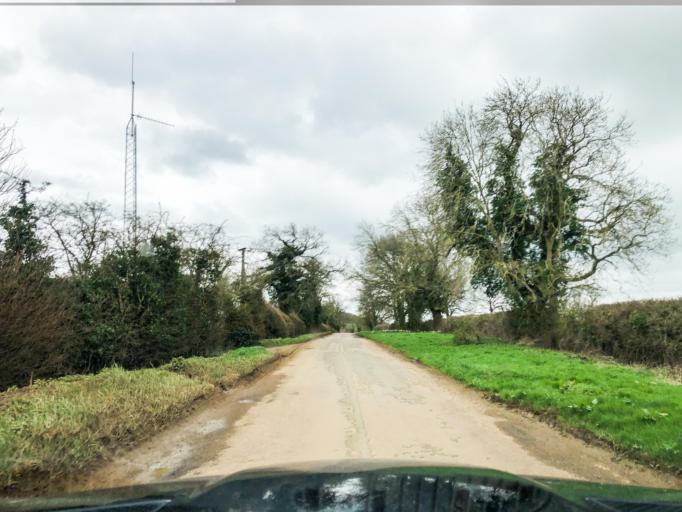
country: GB
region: England
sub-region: Oxfordshire
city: Hook Norton
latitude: 52.0700
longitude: -1.4753
